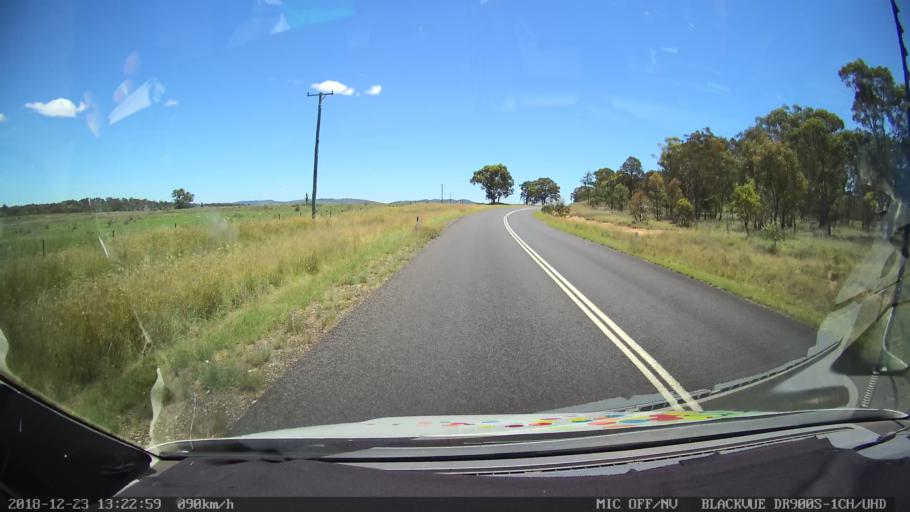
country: AU
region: New South Wales
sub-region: Armidale Dumaresq
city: Armidale
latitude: -30.4811
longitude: 151.4134
